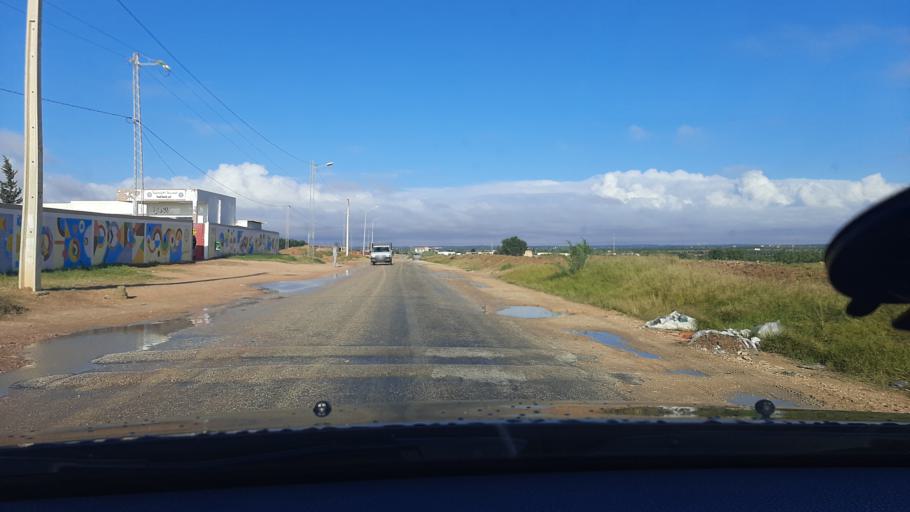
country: TN
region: Safaqis
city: Sfax
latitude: 34.8816
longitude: 10.6317
